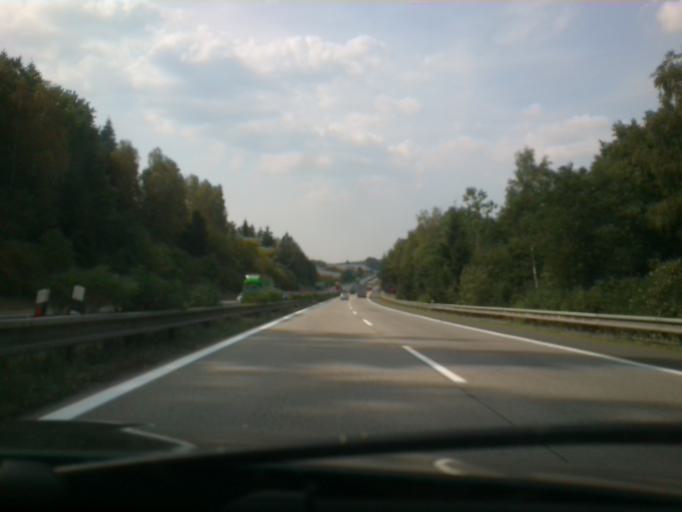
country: CZ
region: Central Bohemia
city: Divisov
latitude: 49.8139
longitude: 14.8803
